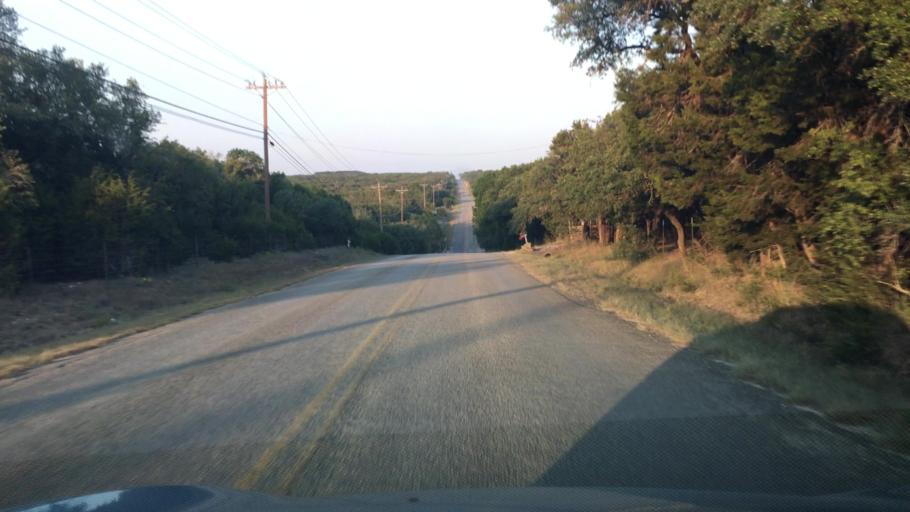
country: US
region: Texas
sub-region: Hays County
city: Dripping Springs
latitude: 30.1532
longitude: -98.0241
